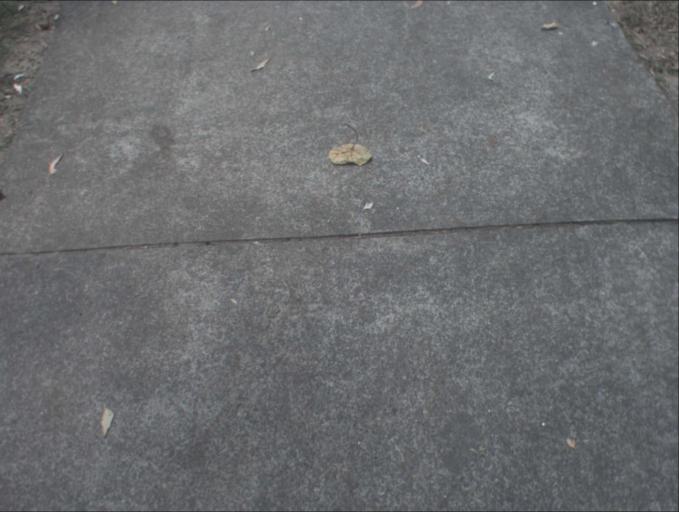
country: AU
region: Queensland
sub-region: Logan
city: Slacks Creek
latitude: -27.6458
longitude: 153.1735
